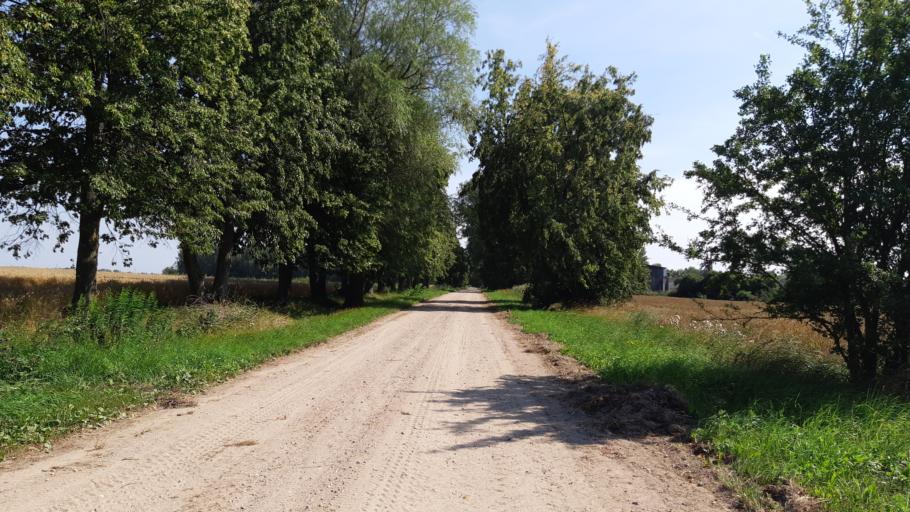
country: LT
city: Virbalis
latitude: 54.6388
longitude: 22.8222
